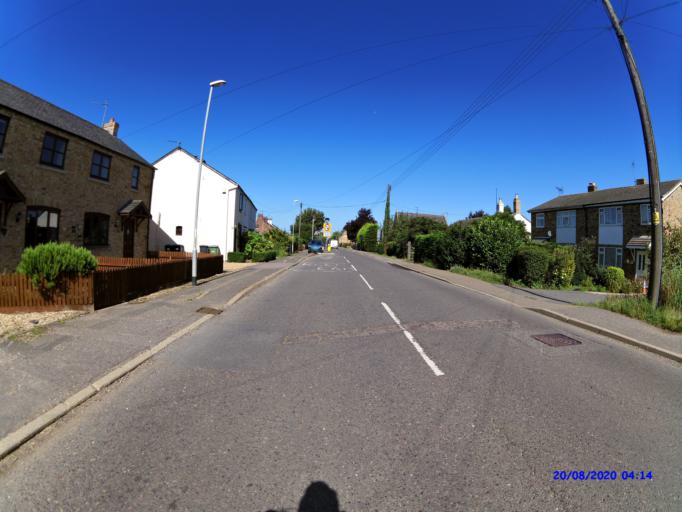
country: GB
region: England
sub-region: Cambridgeshire
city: Ramsey
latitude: 52.4846
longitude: -0.1082
